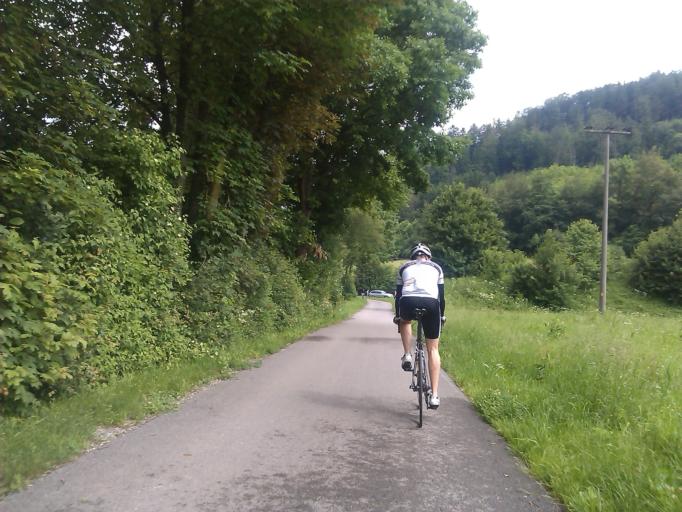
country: DE
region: Baden-Wuerttemberg
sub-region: Regierungsbezirk Stuttgart
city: Gaildorf
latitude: 48.9744
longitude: 9.7946
